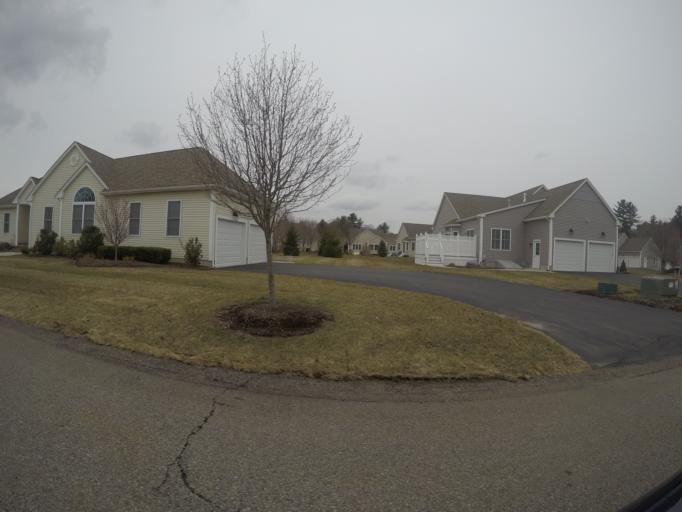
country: US
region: Massachusetts
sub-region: Bristol County
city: Easton
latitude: 42.0316
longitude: -71.1534
